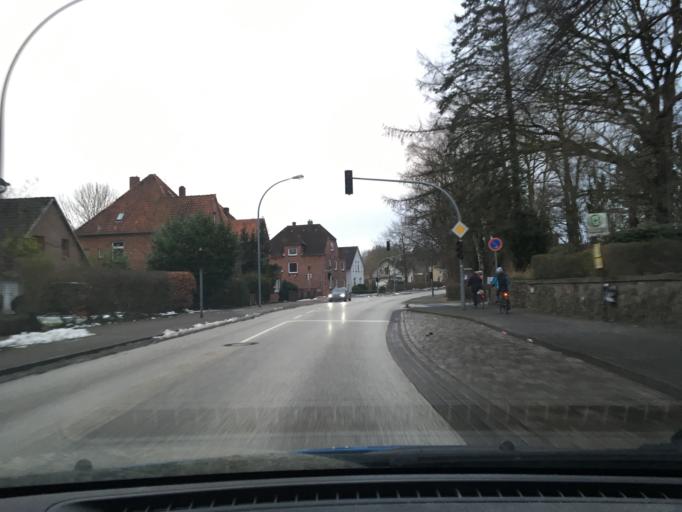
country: DE
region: Schleswig-Holstein
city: Itzehoe
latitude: 53.9370
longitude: 9.4993
